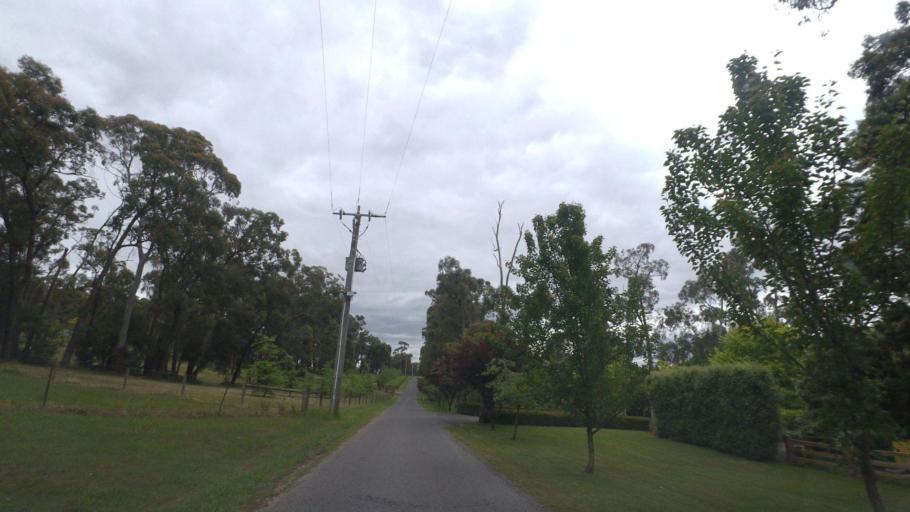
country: AU
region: Victoria
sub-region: Yarra Ranges
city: Mount Evelyn
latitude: -37.7562
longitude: 145.4213
